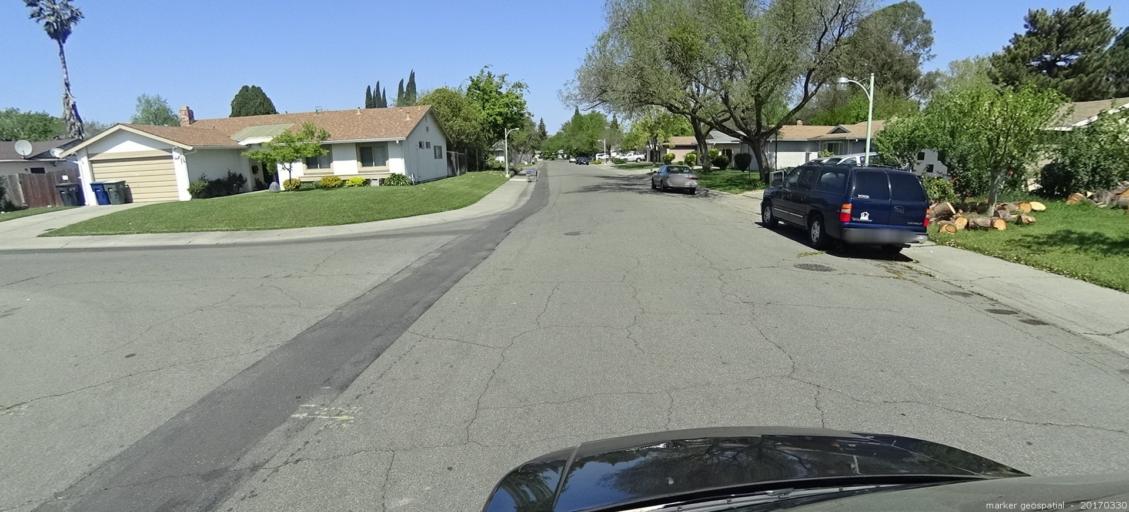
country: US
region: California
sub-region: Sacramento County
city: Florin
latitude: 38.4686
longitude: -121.4287
